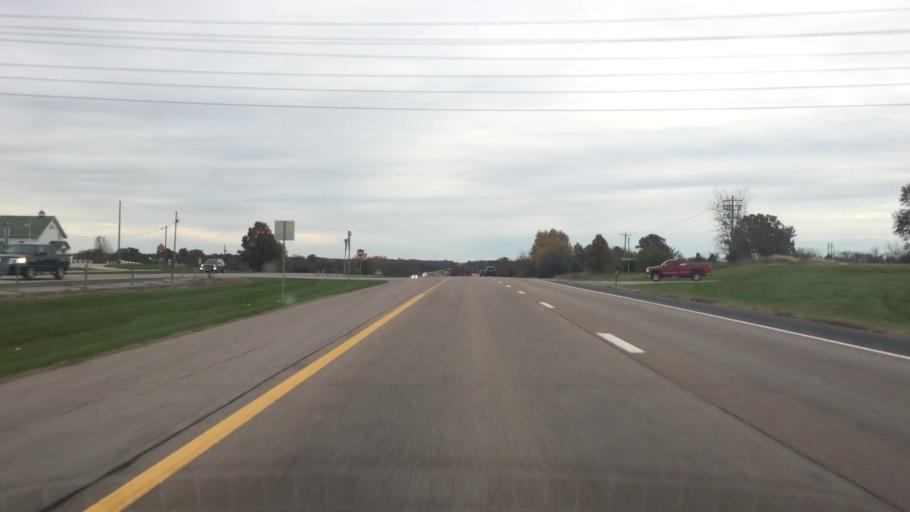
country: US
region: Missouri
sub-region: Boone County
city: Ashland
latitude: 38.7981
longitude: -92.2514
